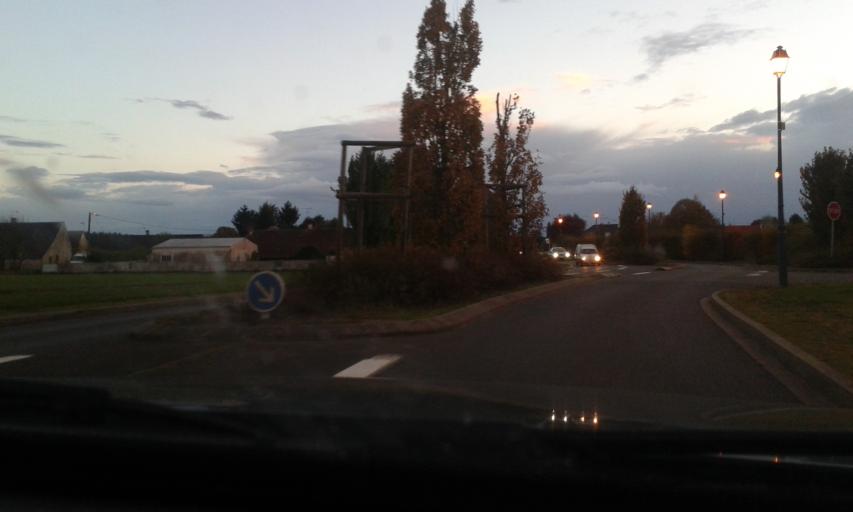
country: FR
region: Centre
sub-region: Departement du Loiret
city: Huisseau-sur-Mauves
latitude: 47.9008
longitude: 1.7045
